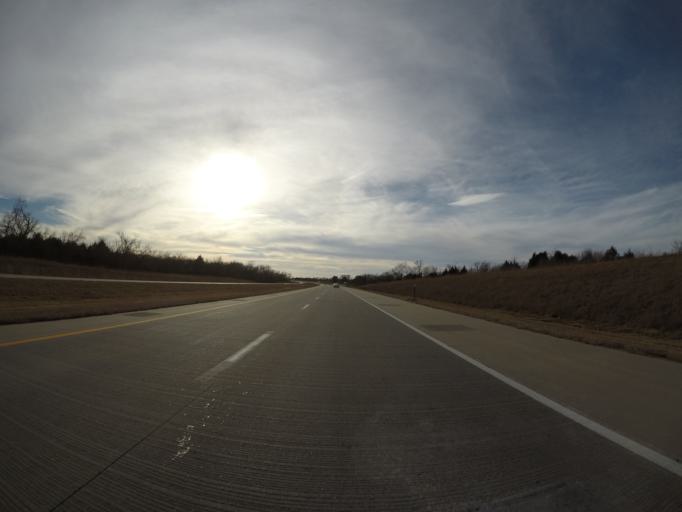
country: US
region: Kansas
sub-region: Franklin County
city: Ottawa
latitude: 38.6612
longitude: -95.1803
